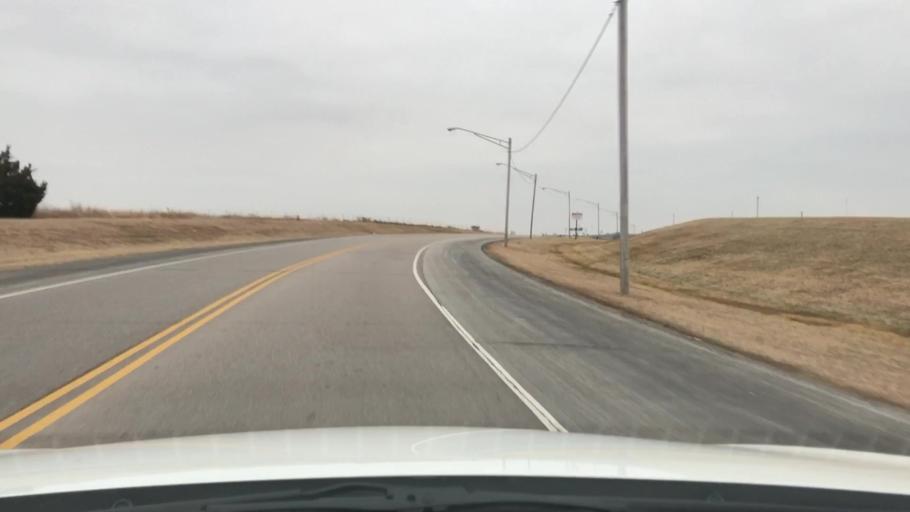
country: US
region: Oklahoma
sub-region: Carter County
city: Ardmore
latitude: 34.1860
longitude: -97.1686
